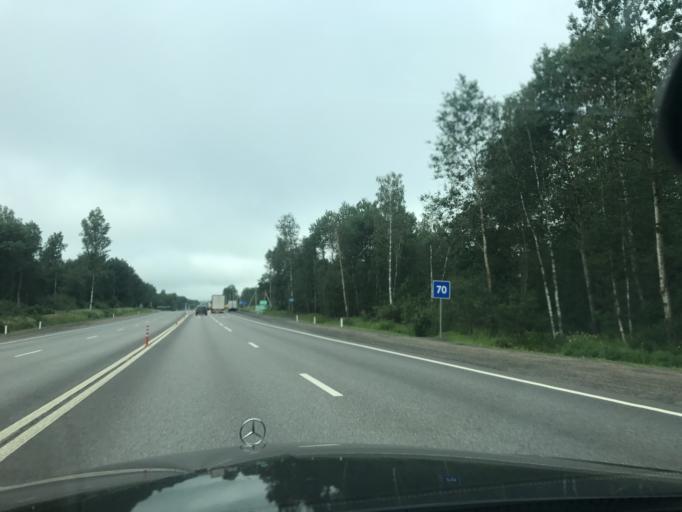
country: RU
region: Smolensk
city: Vyaz'ma
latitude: 55.2708
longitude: 34.4044
